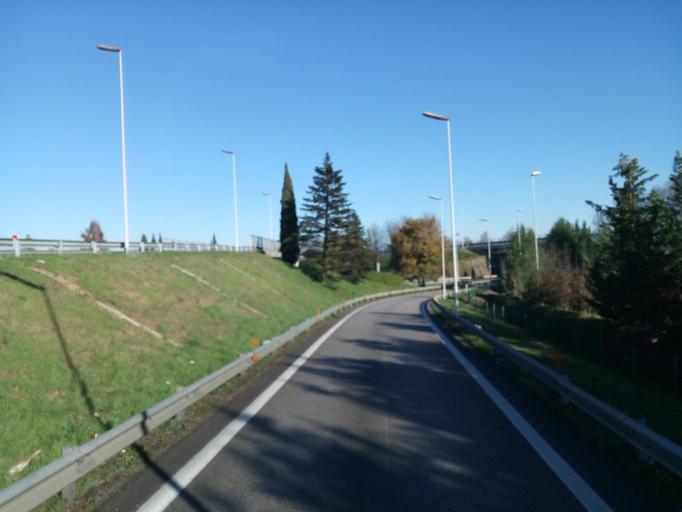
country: IT
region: Veneto
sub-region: Provincia di Vicenza
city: Lisiera
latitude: 45.5798
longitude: 11.5989
